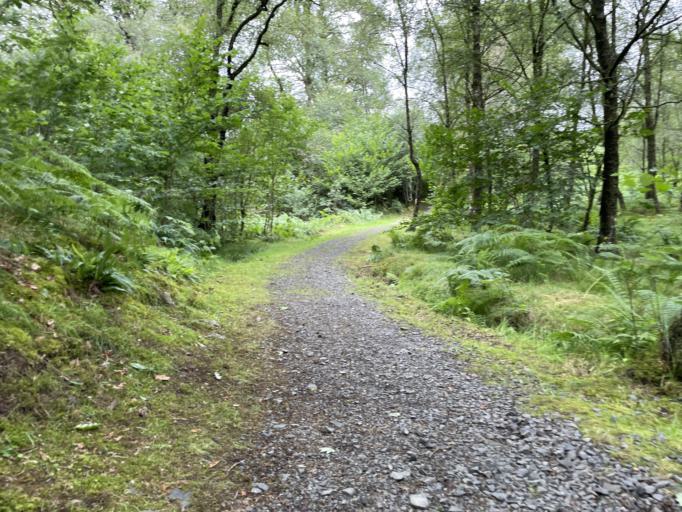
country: GB
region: Scotland
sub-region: Dumfries and Galloway
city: Newton Stewart
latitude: 55.0810
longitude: -4.5042
